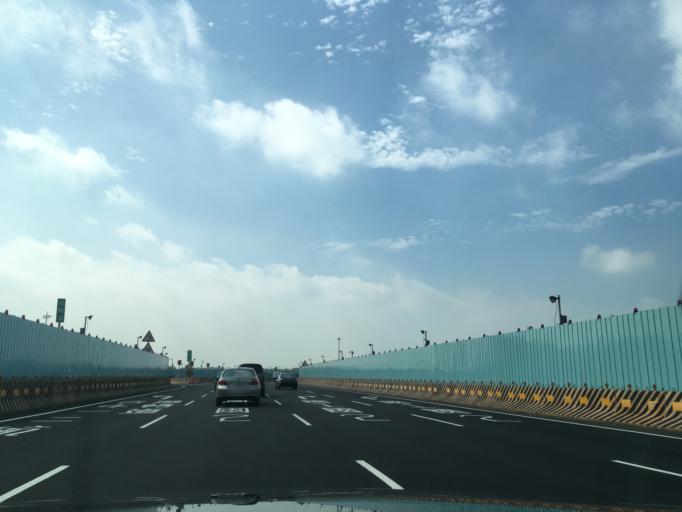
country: TW
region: Taiwan
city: Taoyuan City
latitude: 25.0750
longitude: 121.2290
